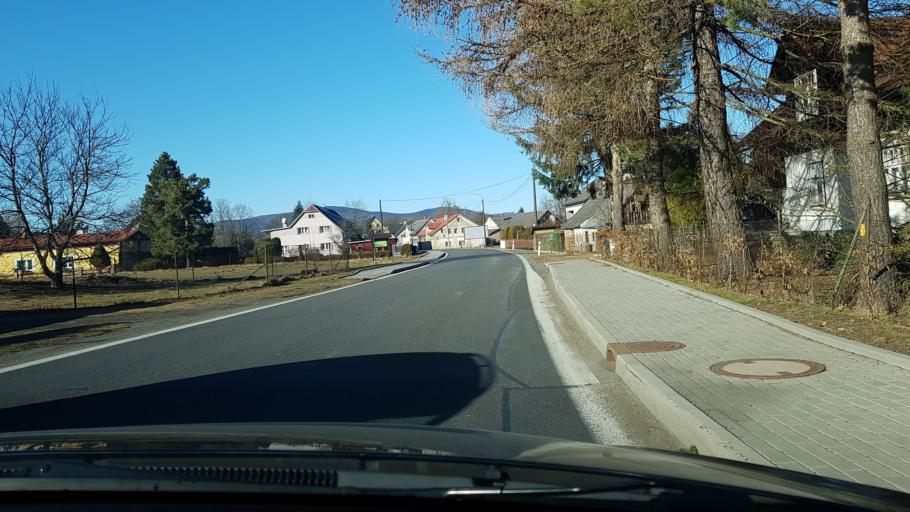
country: CZ
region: Olomoucky
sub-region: Okres Jesenik
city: Jesenik
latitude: 50.1814
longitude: 17.1986
